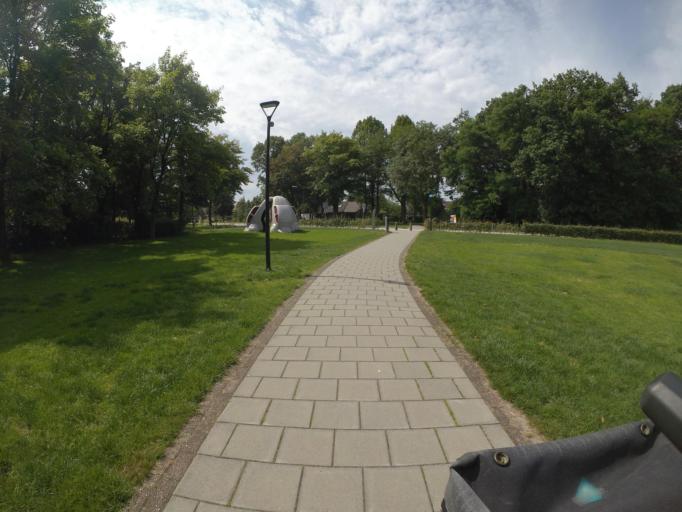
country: NL
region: North Brabant
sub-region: Bergeijk
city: Bergeyk
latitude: 51.3244
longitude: 5.3640
